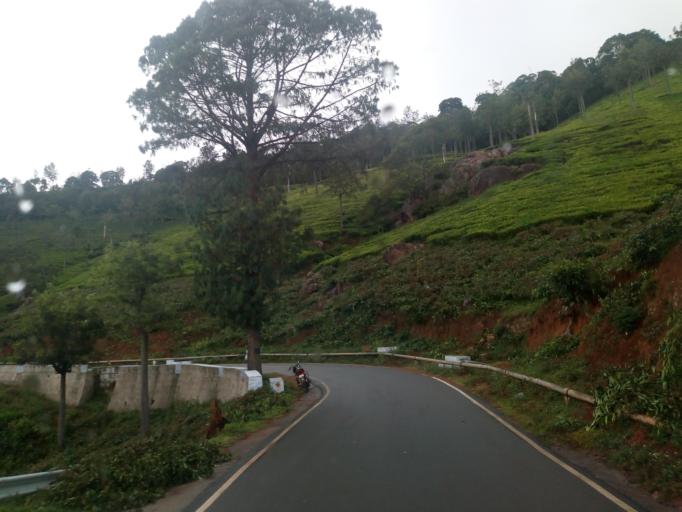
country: IN
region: Tamil Nadu
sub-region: Nilgiri
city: Wellington
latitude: 11.3545
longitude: 76.8321
